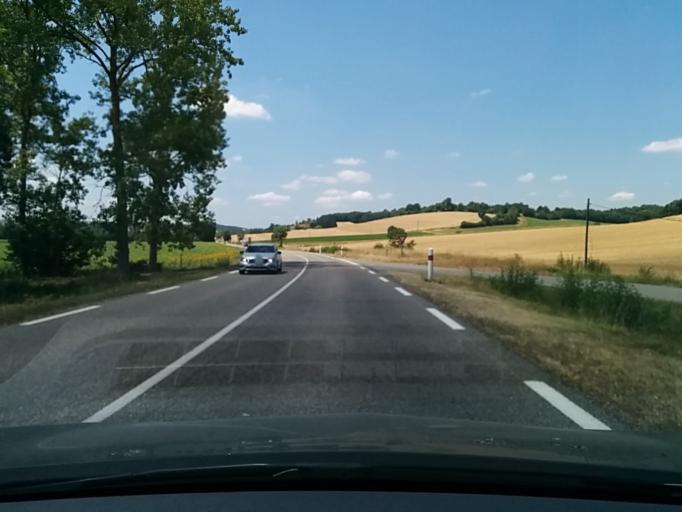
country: FR
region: Midi-Pyrenees
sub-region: Departement du Gers
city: Jegun
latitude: 43.6905
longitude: 0.4776
